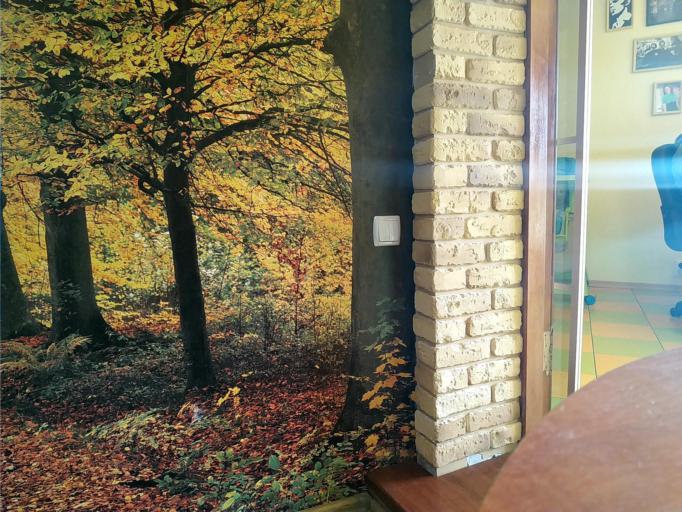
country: RU
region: Smolensk
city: Safonovo
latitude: 55.1056
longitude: 33.1323
